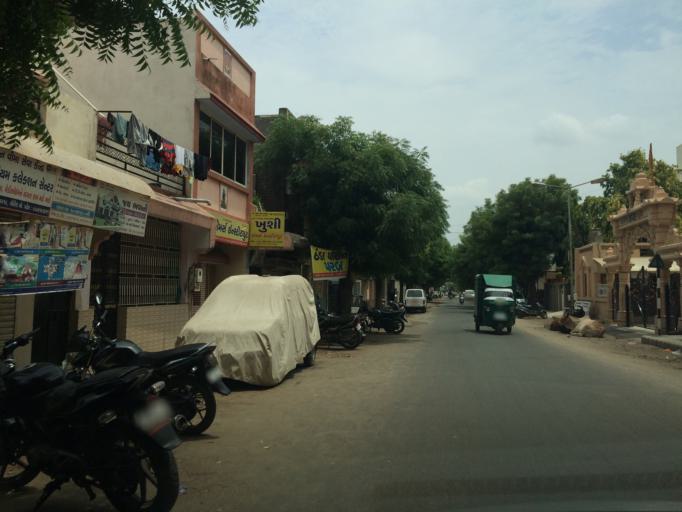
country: IN
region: Gujarat
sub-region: Ahmadabad
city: Ahmedabad
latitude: 23.0803
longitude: 72.5638
